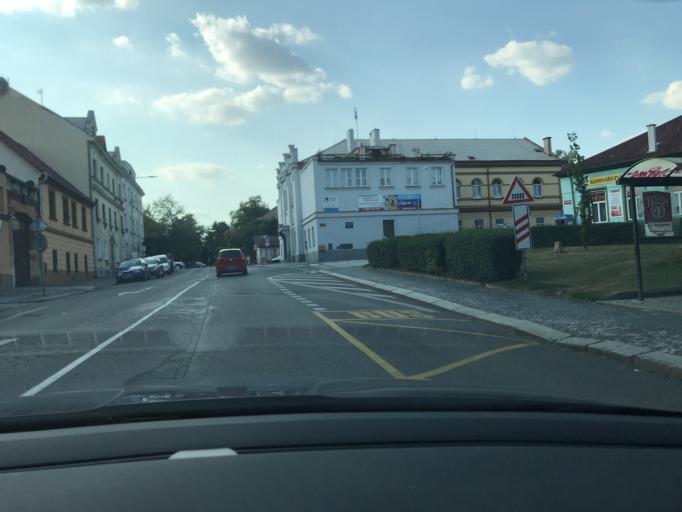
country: CZ
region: Central Bohemia
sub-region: Okres Kladno
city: Slany
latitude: 50.2330
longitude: 14.0807
